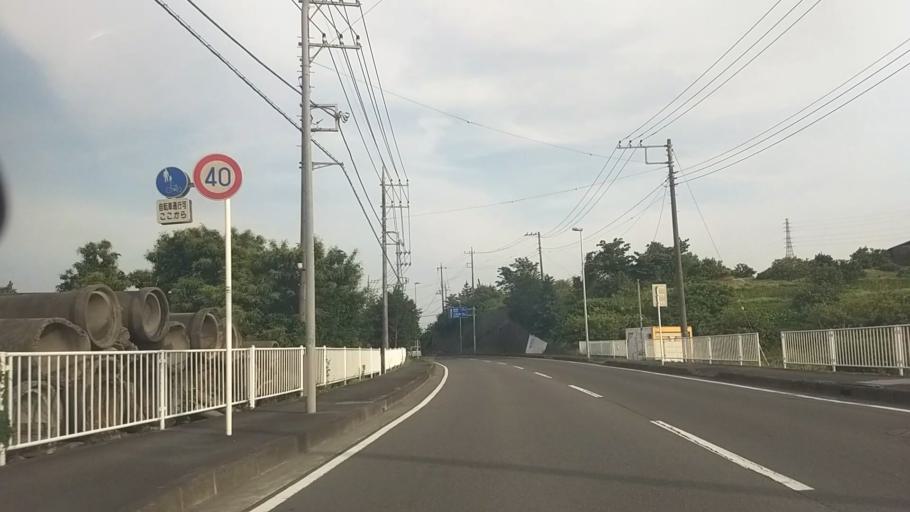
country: JP
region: Kanagawa
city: Odawara
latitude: 35.3456
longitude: 139.0983
